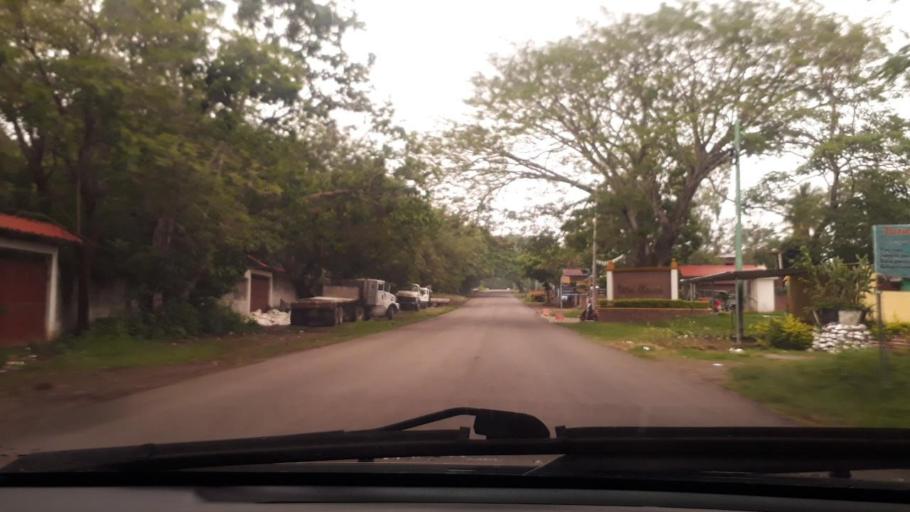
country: GT
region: Jutiapa
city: Jalpatagua
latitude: 14.1175
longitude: -89.9759
